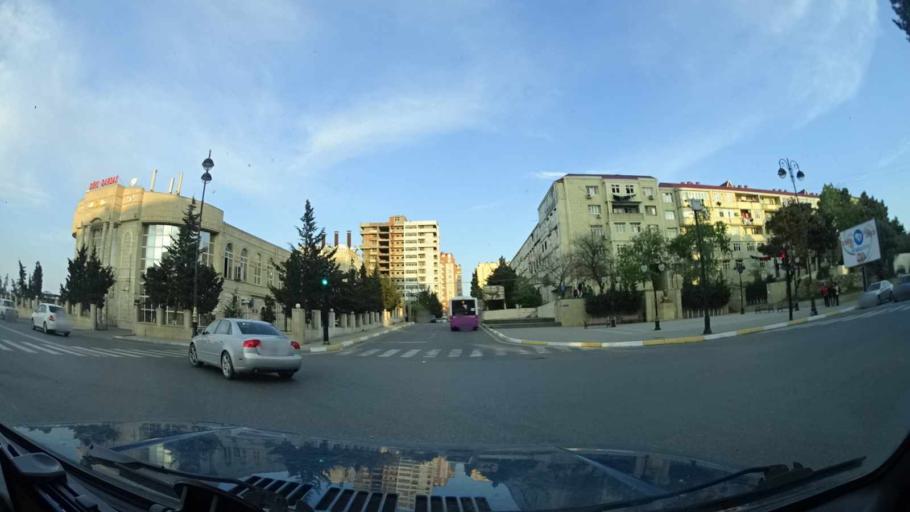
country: AZ
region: Sumqayit
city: Corat
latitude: 40.5819
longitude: 49.6879
